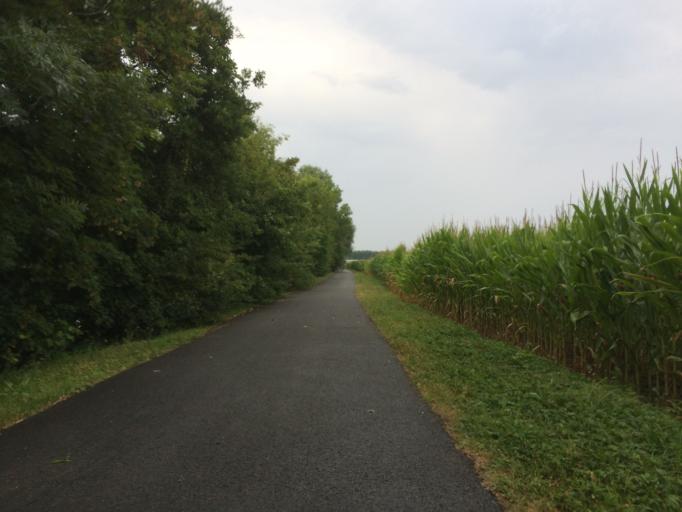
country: FR
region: Picardie
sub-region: Departement de l'Oise
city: Jaux
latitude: 49.3756
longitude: 2.7773
